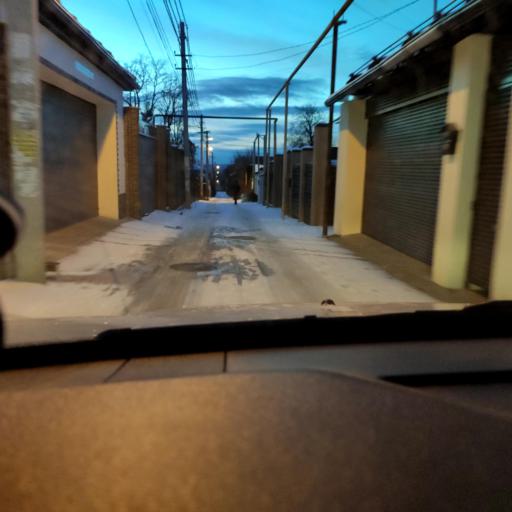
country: RU
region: Samara
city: Samara
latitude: 53.2592
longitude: 50.1959
